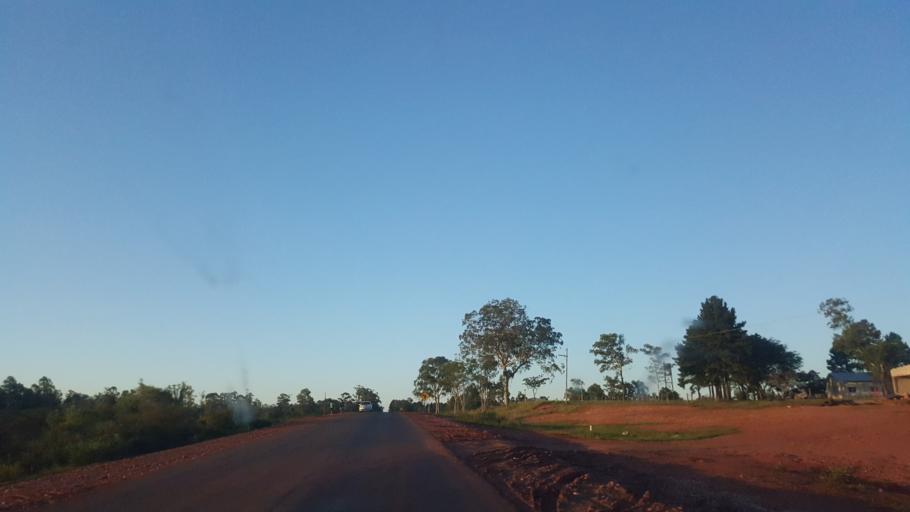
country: AR
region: Corrientes
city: Santo Tome
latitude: -28.5217
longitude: -56.0564
